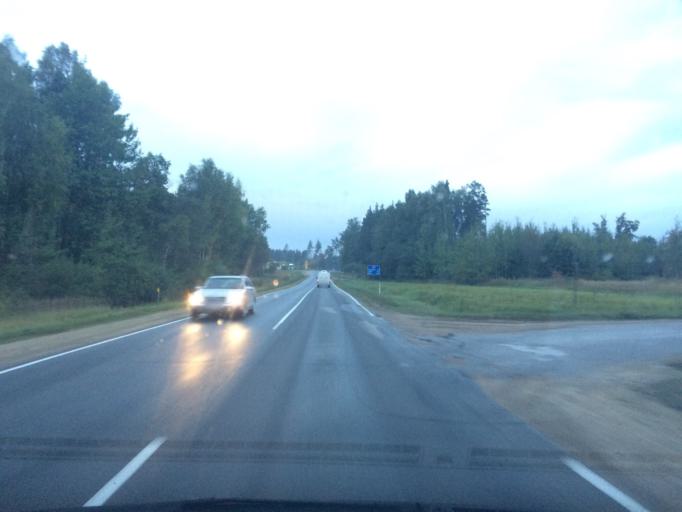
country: LV
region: Jekabpils Rajons
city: Jekabpils
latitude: 56.5319
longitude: 25.8219
